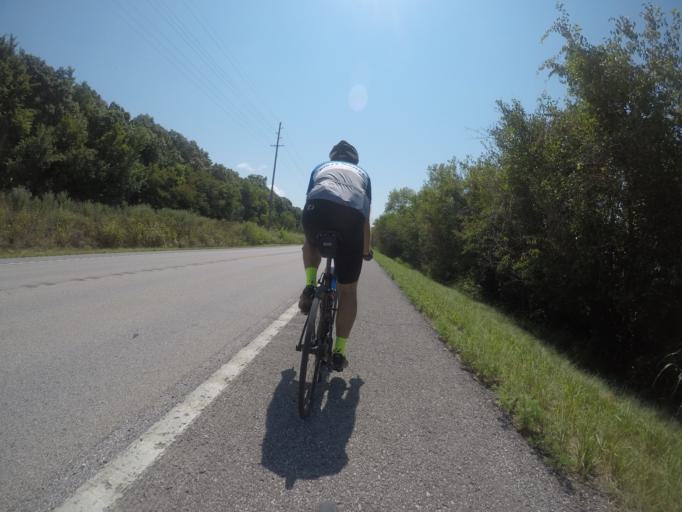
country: US
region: Missouri
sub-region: Platte County
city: Weston
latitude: 39.4825
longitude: -94.9917
